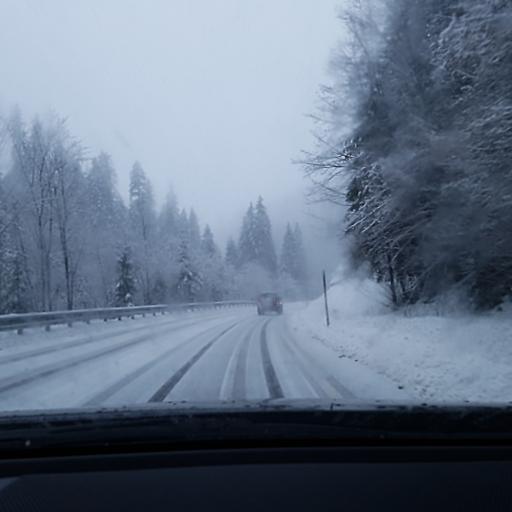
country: AT
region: Salzburg
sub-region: Politischer Bezirk Hallein
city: Abtenau
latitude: 47.5788
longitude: 13.4101
